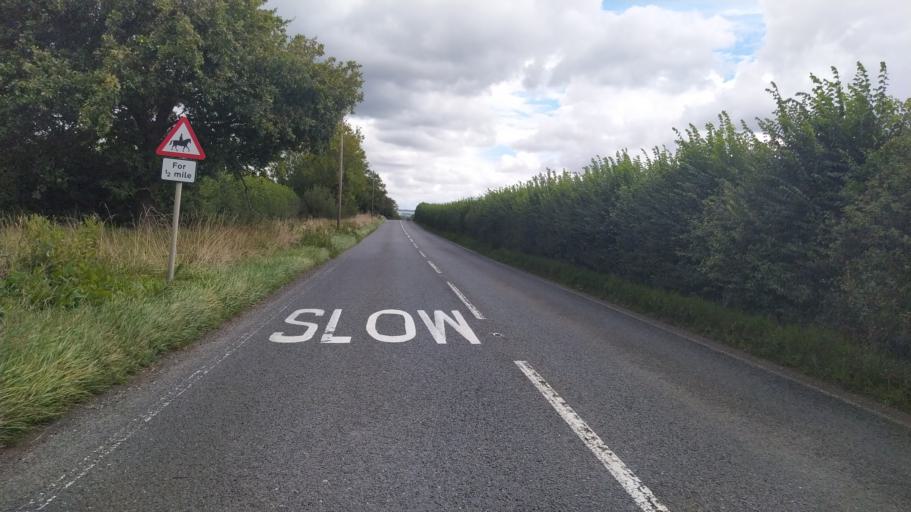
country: GB
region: England
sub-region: Dorset
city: Sturminster Newton
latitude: 50.9184
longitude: -2.3340
